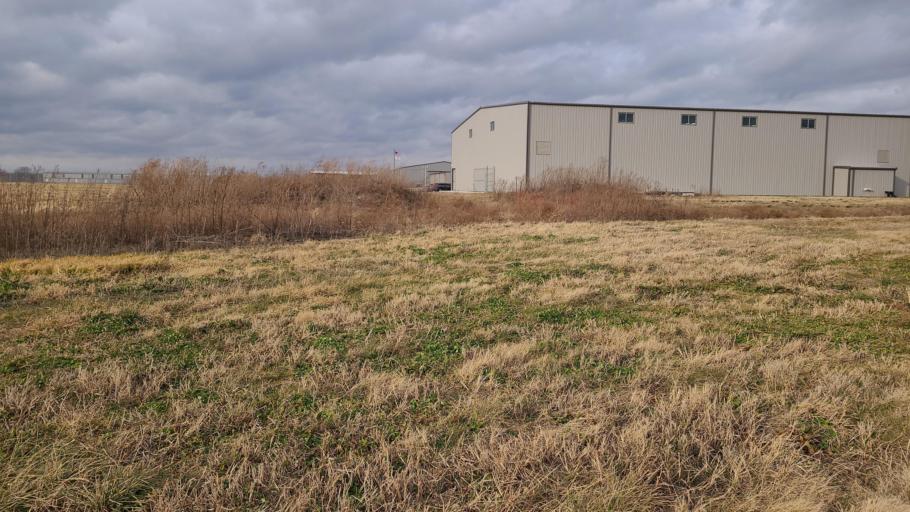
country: US
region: Kansas
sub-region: Douglas County
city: Lawrence
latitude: 39.0048
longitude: -95.2139
